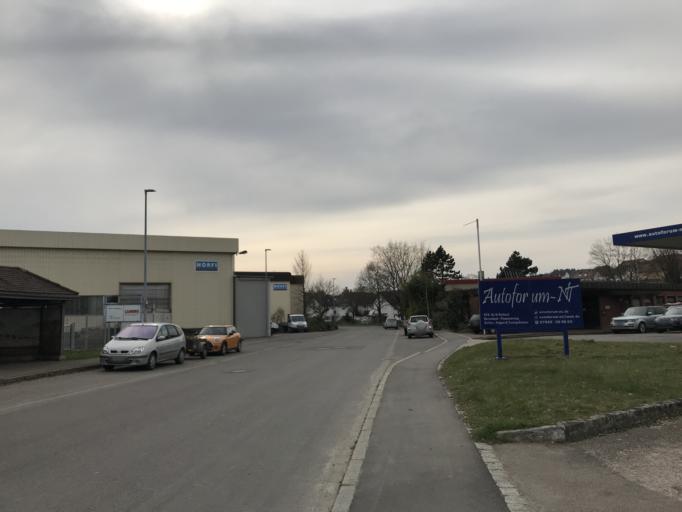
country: DE
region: Baden-Wuerttemberg
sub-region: Regierungsbezirk Stuttgart
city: Unterensingen
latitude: 48.6535
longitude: 9.3566
